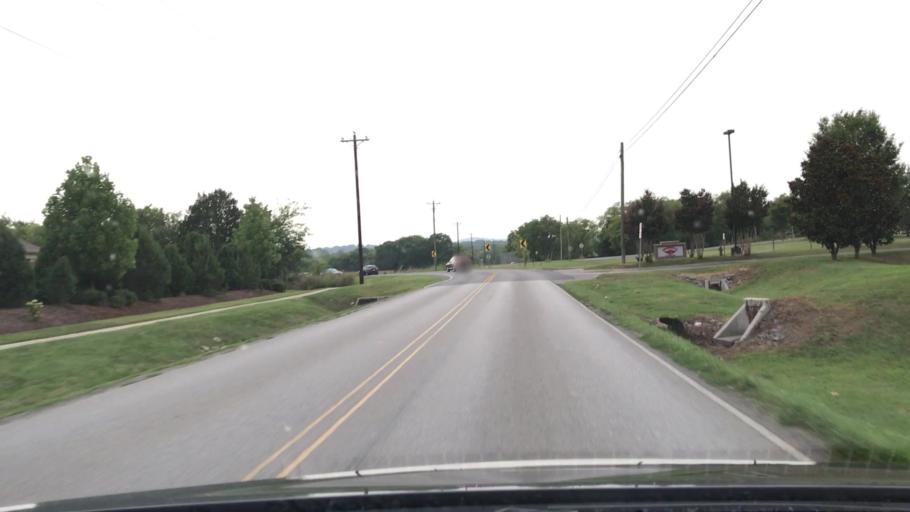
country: US
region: Tennessee
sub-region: Williamson County
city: Nolensville
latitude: 35.9531
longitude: -86.6612
